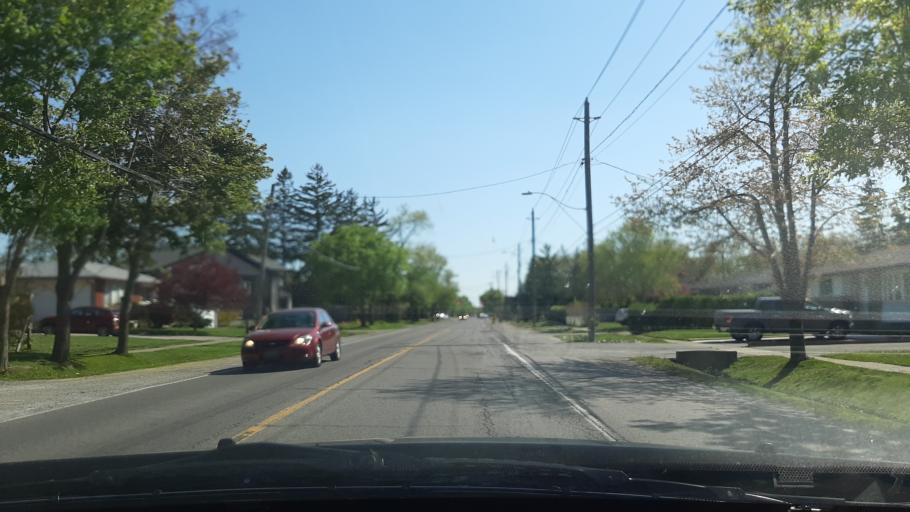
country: CA
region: Ontario
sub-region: Regional Municipality of Niagara
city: St. Catharines
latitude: 43.2031
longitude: -79.2210
